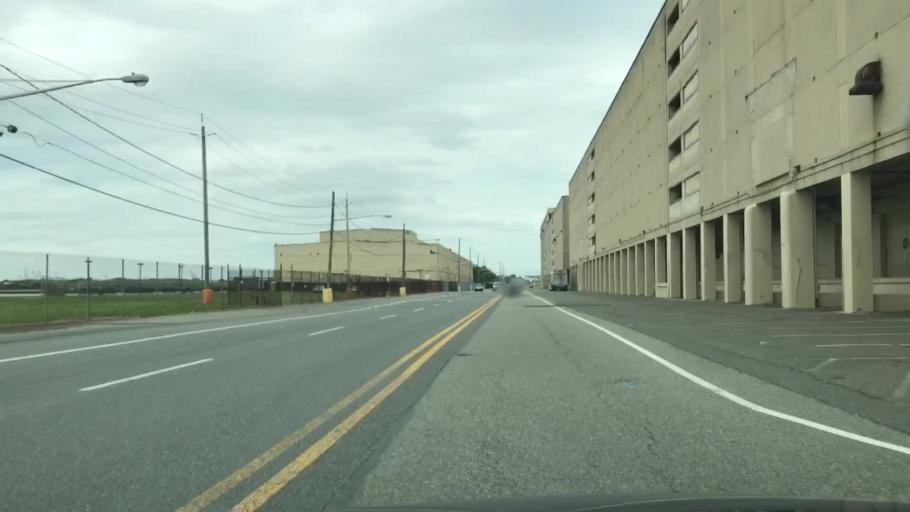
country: US
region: New Jersey
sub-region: Hudson County
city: Bayonne
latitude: 40.6653
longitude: -74.0803
